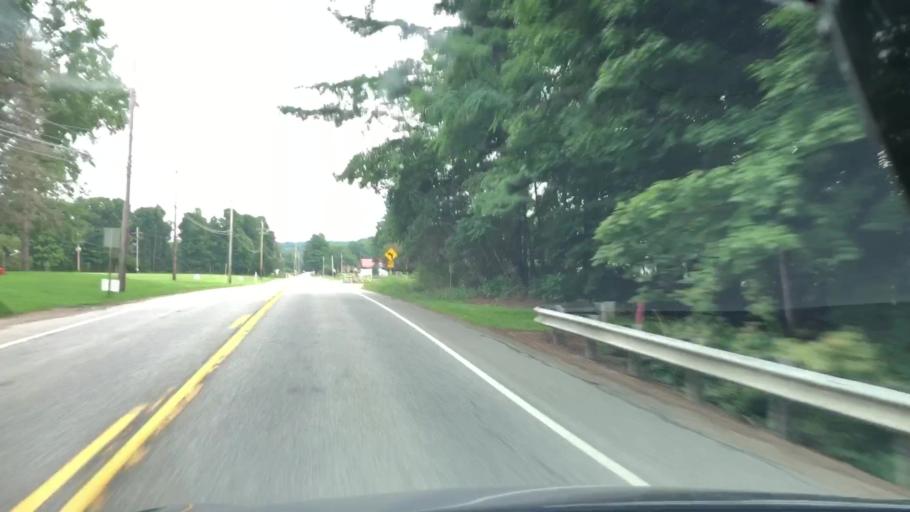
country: US
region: Pennsylvania
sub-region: Erie County
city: Union City
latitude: 42.0104
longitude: -79.8151
